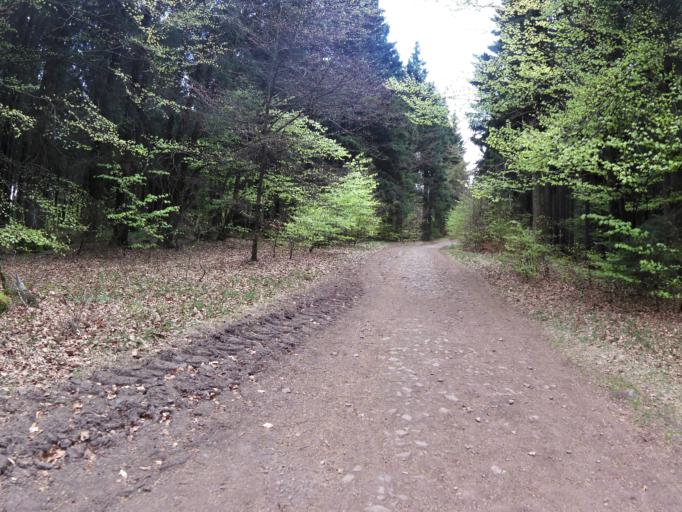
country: DE
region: Thuringia
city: Friedrichroda
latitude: 50.8237
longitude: 10.5403
